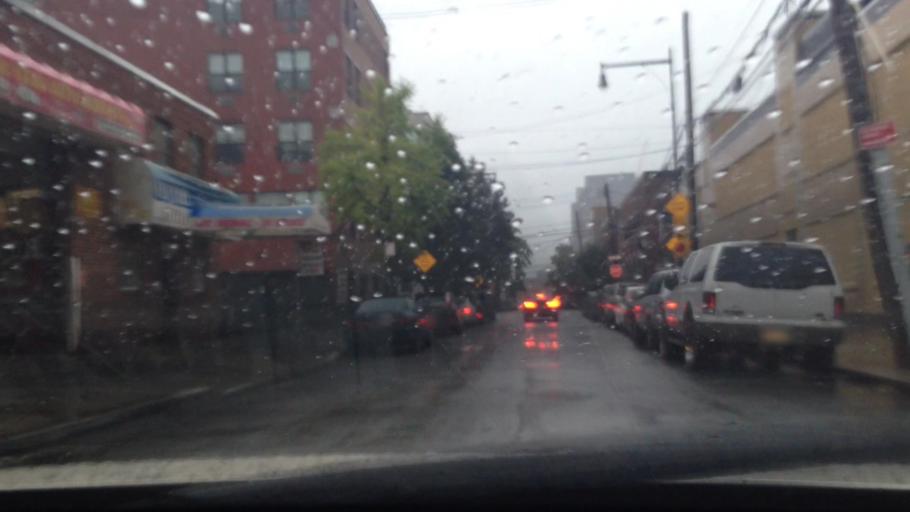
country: US
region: New York
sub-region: Queens County
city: Long Island City
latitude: 40.7438
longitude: -73.9562
